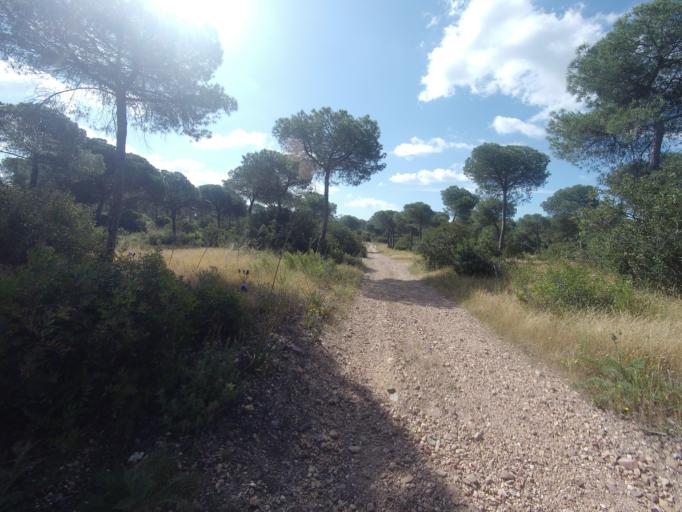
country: ES
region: Andalusia
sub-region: Provincia de Huelva
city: Aljaraque
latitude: 37.2398
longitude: -7.0291
